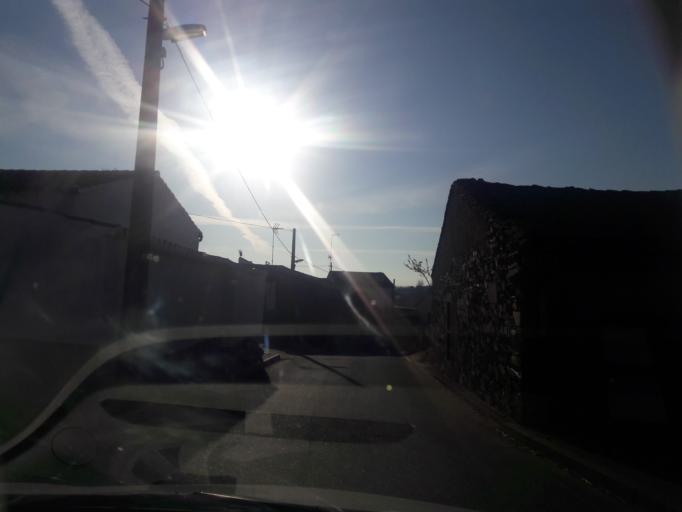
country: ES
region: Castille and Leon
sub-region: Provincia de Salamanca
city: Montejo
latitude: 40.6310
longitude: -5.6211
